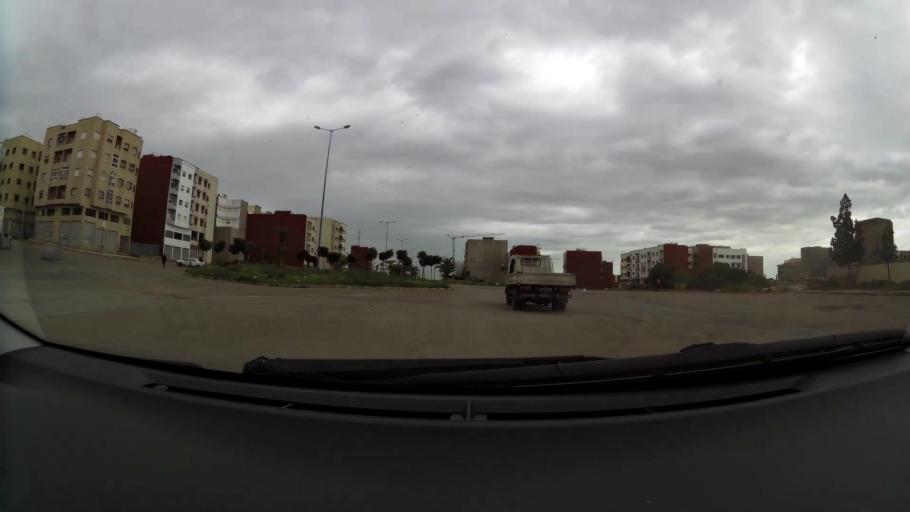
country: MA
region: Grand Casablanca
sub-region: Mediouna
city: Tit Mellil
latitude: 33.5600
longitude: -7.5307
